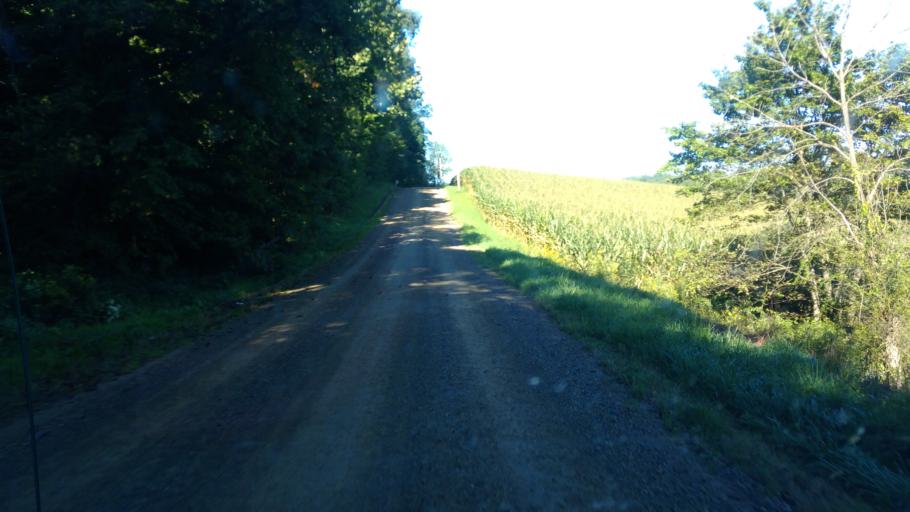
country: US
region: Ohio
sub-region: Knox County
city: Gambier
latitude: 40.4381
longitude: -82.4072
